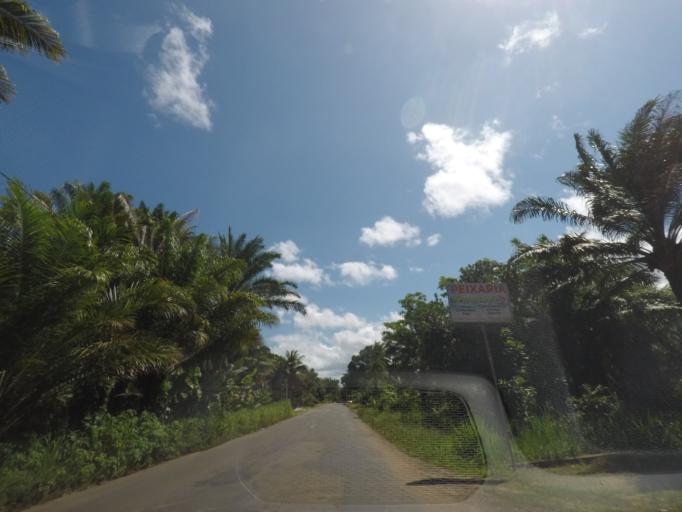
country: BR
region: Bahia
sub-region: Taperoa
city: Taperoa
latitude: -13.4902
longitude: -39.0926
